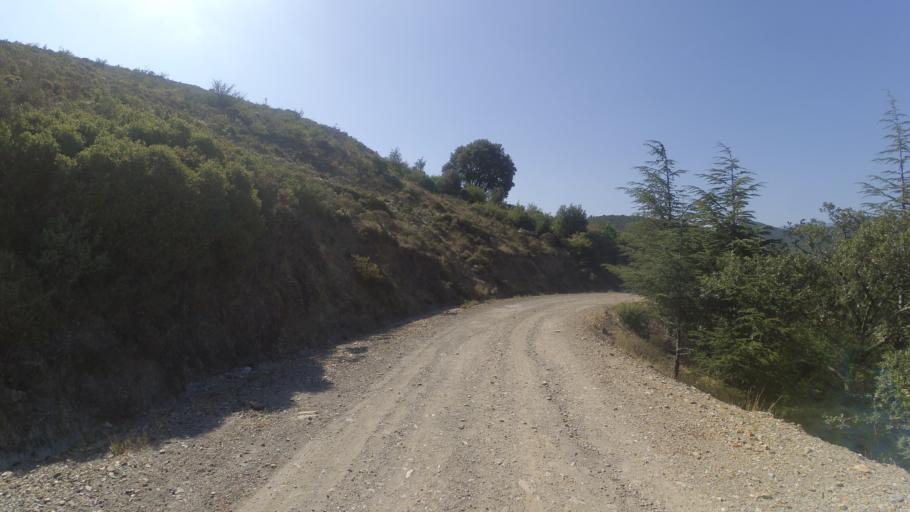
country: FR
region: Languedoc-Roussillon
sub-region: Departement des Pyrenees-Orientales
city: Millas
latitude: 42.6260
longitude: 2.6752
